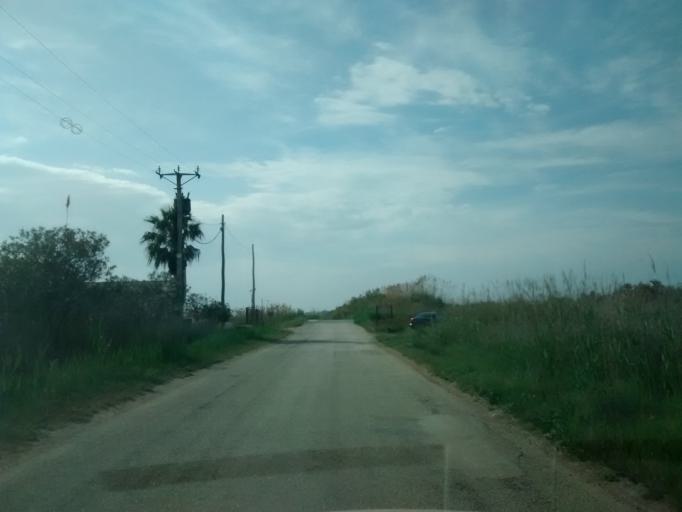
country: ES
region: Catalonia
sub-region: Provincia de Tarragona
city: Deltebre
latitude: 40.6879
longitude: 0.8487
